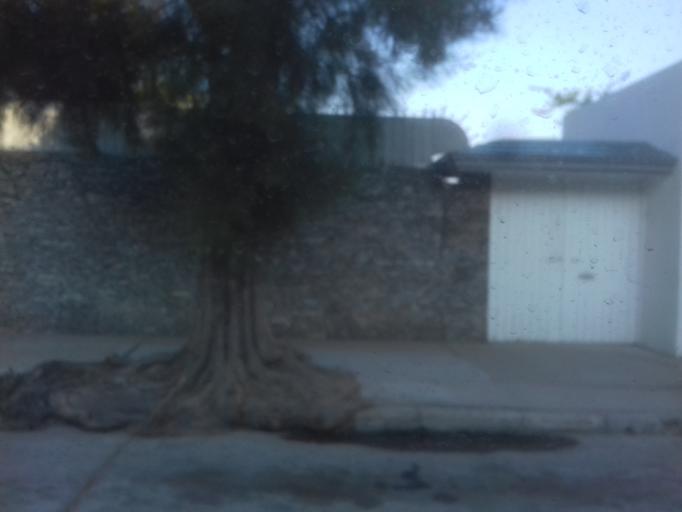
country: MX
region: Aguascalientes
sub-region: Aguascalientes
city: Aguascalientes
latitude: 21.8636
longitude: -102.2899
